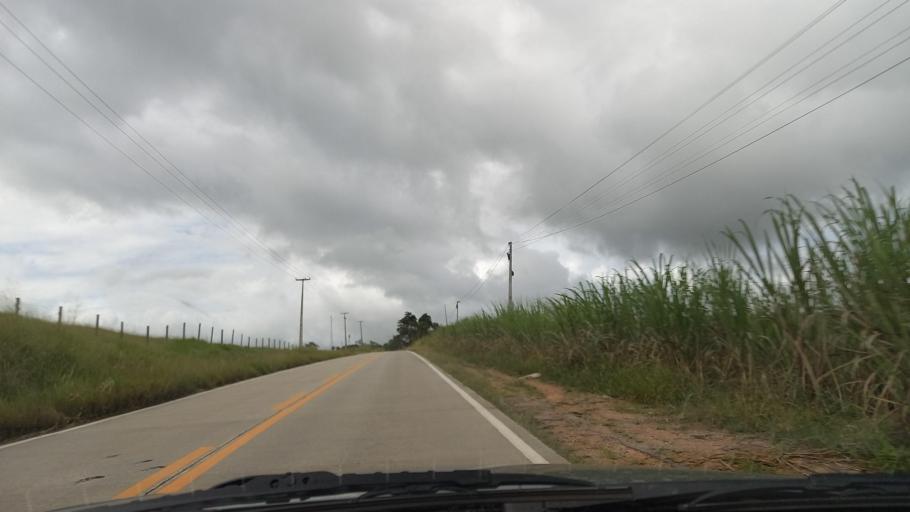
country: BR
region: Pernambuco
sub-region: Quipapa
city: Quipapa
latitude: -8.7995
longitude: -35.9991
